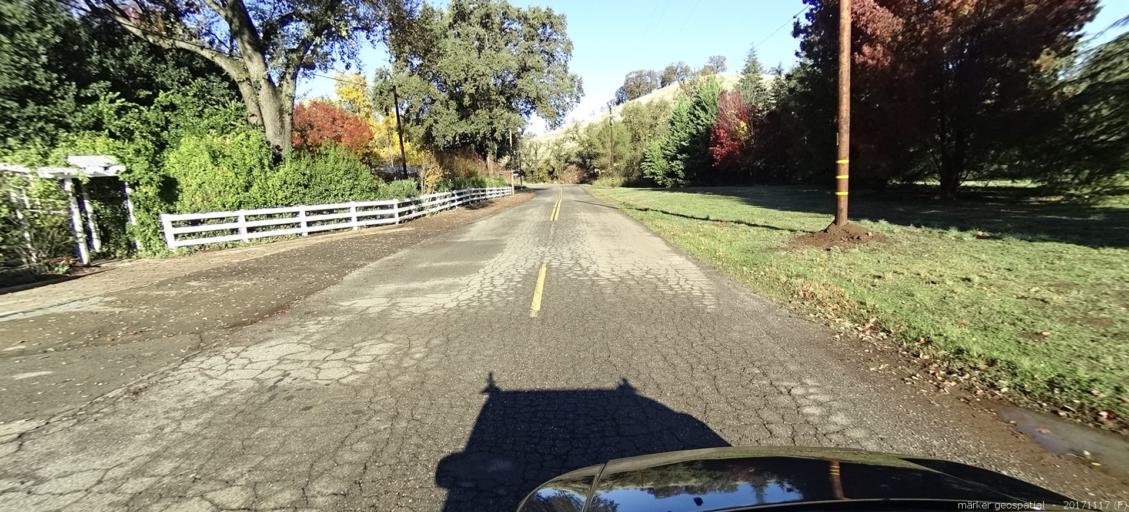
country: US
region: California
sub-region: Shasta County
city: Cottonwood
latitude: 40.3976
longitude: -122.1788
